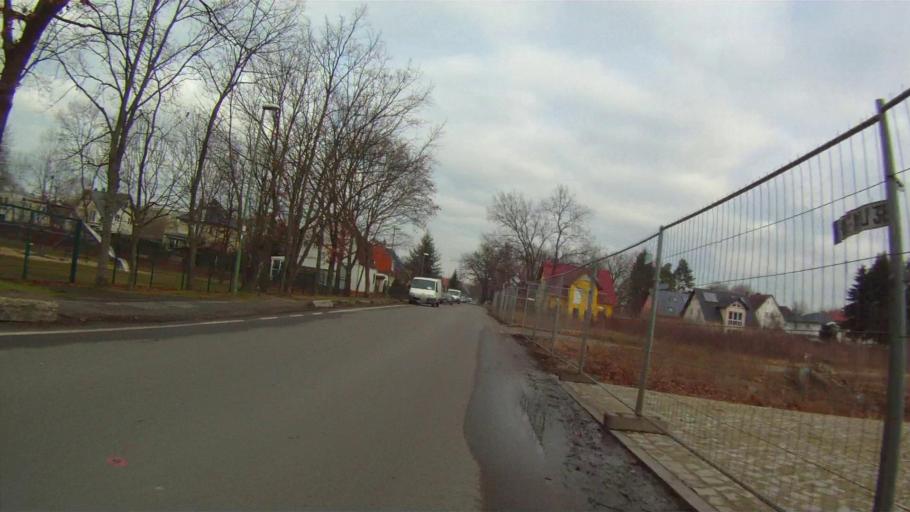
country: DE
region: Berlin
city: Karlshorst
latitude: 52.4921
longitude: 13.5395
